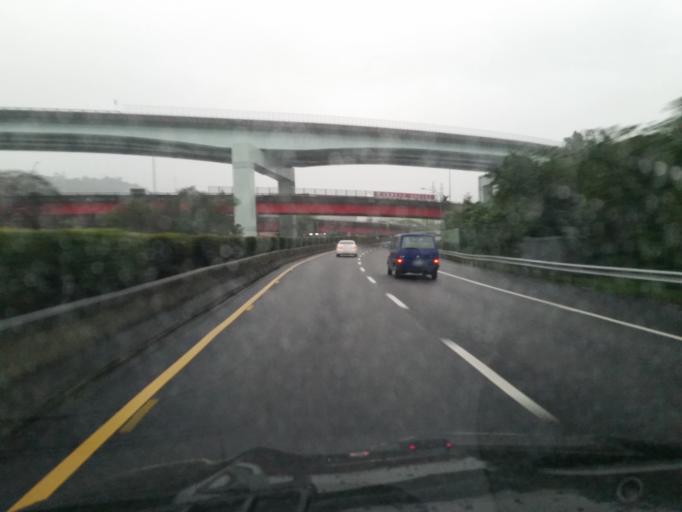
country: TW
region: Taiwan
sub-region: Keelung
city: Keelung
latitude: 25.1064
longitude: 121.7246
